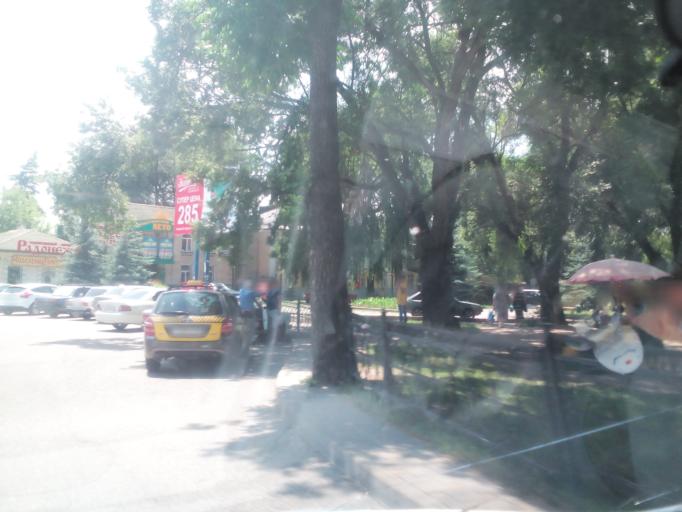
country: RU
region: Stavropol'skiy
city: Pyatigorsk
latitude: 44.0418
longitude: 43.0664
